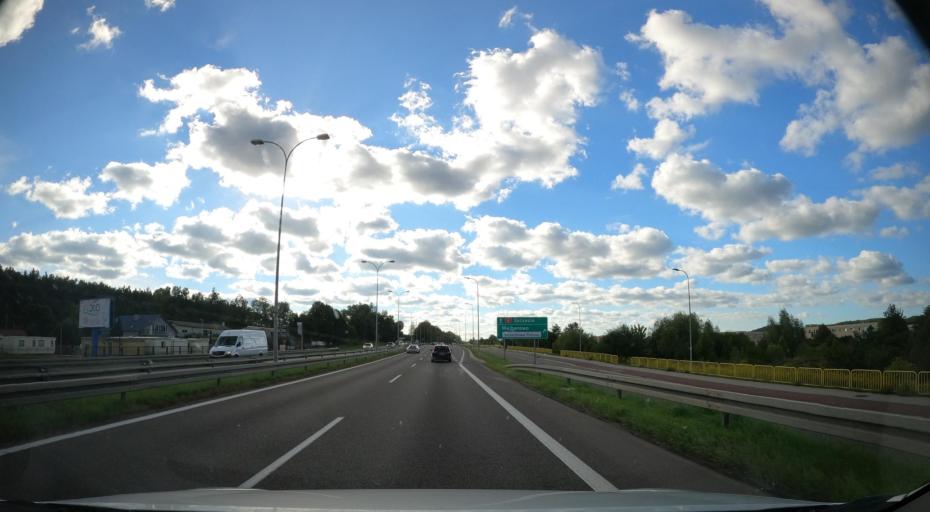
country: PL
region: Pomeranian Voivodeship
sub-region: Powiat wejherowski
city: Wejherowo
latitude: 54.6031
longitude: 18.2889
